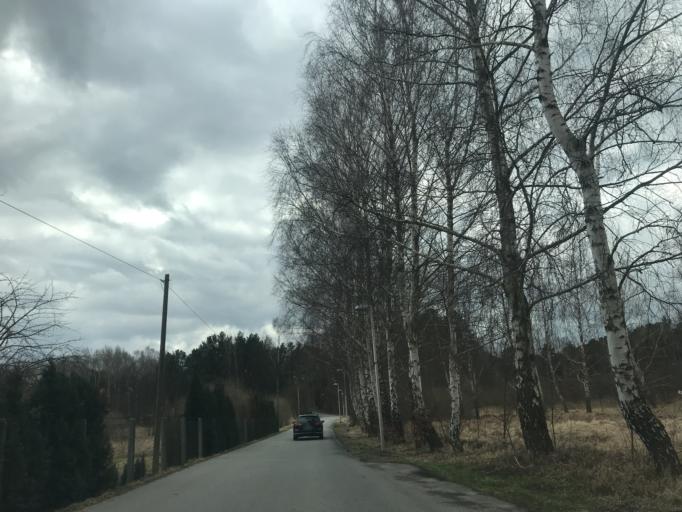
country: DE
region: Brandenburg
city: Zossen
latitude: 52.1430
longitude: 13.4734
